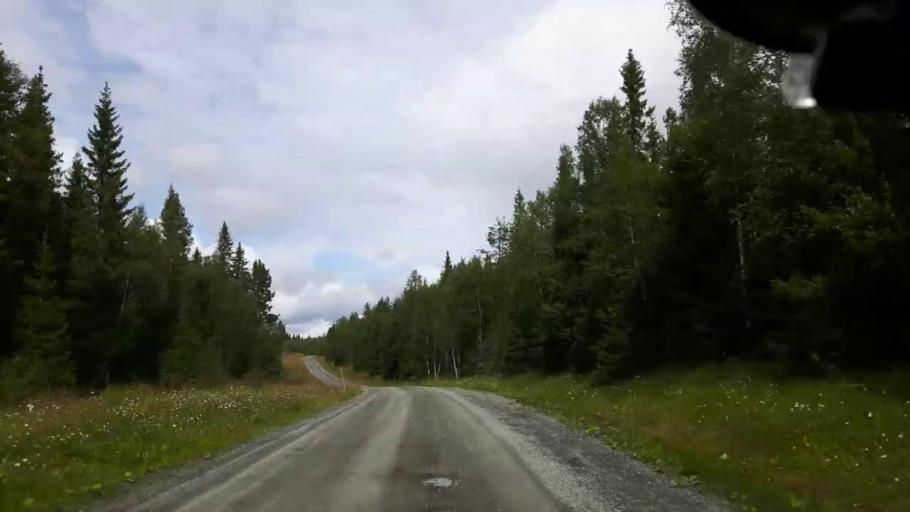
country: SE
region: Jaemtland
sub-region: Krokoms Kommun
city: Valla
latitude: 63.5488
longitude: 13.9165
